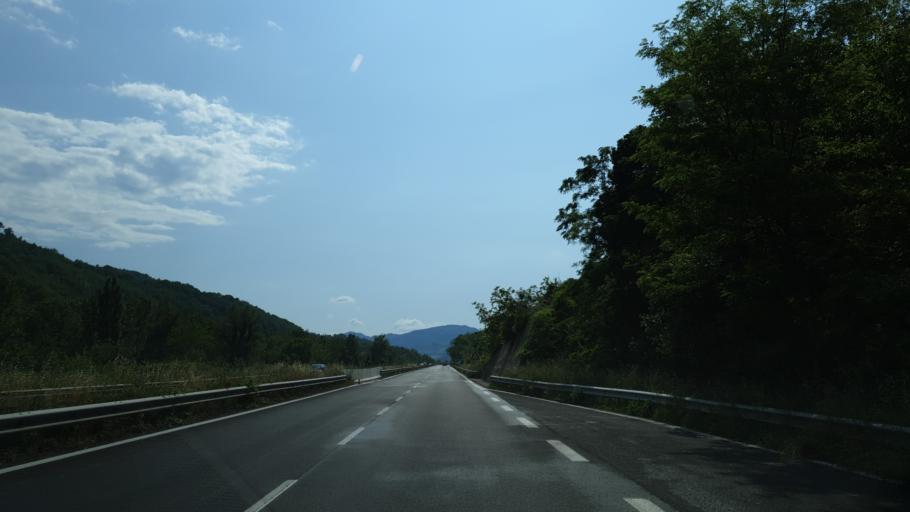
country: IT
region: Emilia-Romagna
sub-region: Forli-Cesena
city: San Piero in Bagno
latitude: 43.8893
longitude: 12.0364
